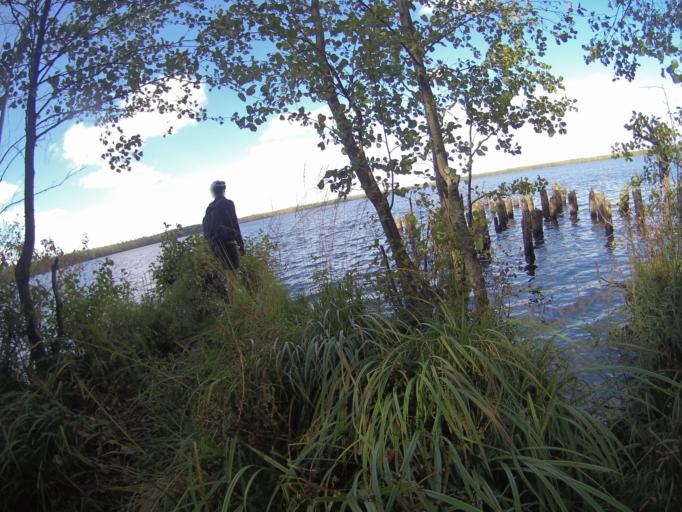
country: RU
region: Vladimir
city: Raduzhnyy
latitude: 55.9334
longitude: 40.1960
